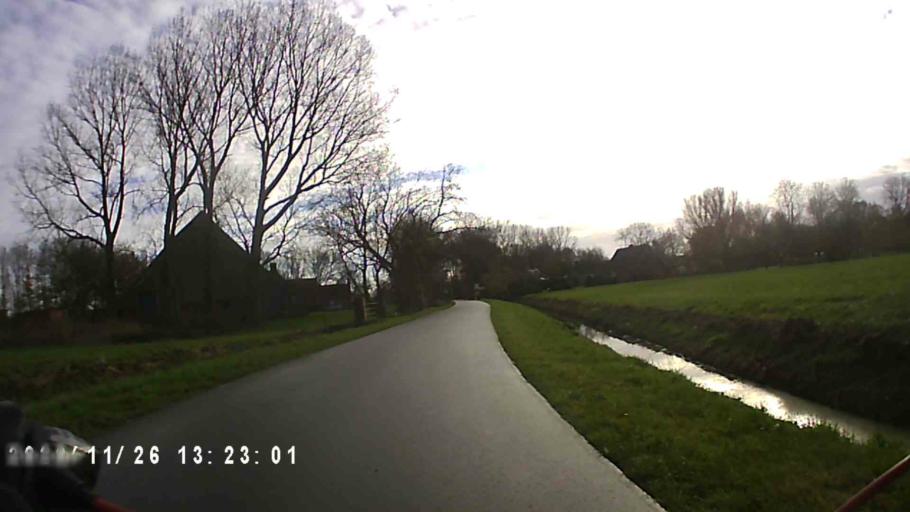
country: NL
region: Groningen
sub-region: Gemeente Delfzijl
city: Delfzijl
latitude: 53.3438
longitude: 6.8960
